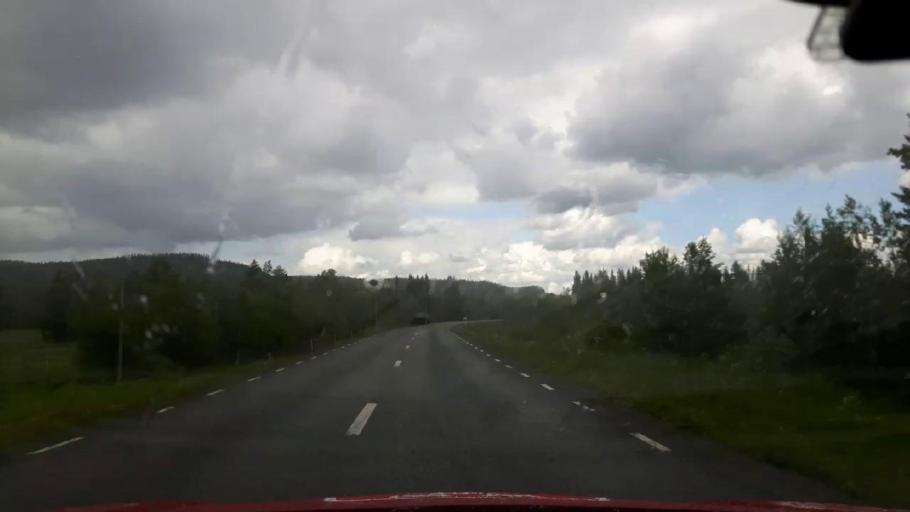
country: SE
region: Jaemtland
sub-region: Krokoms Kommun
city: Krokom
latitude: 63.7443
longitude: 14.2854
